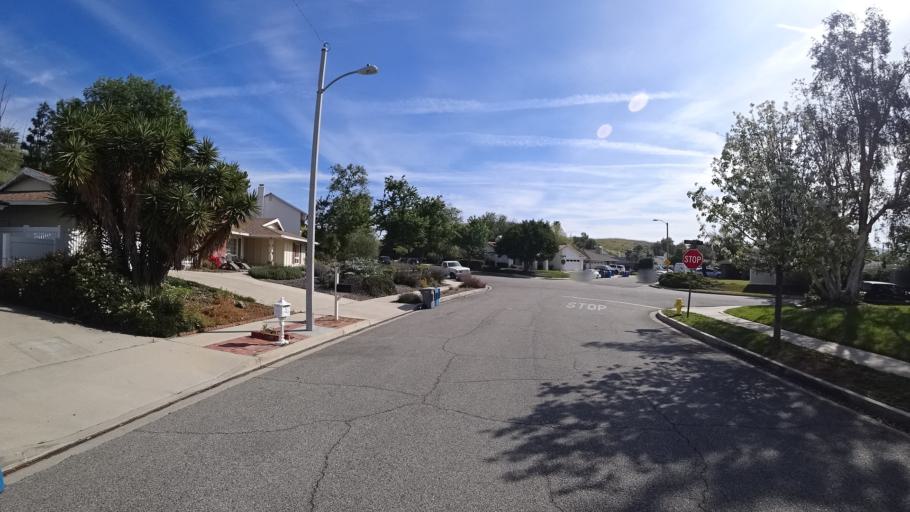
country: US
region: California
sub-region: Ventura County
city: Thousand Oaks
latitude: 34.1996
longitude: -118.8806
